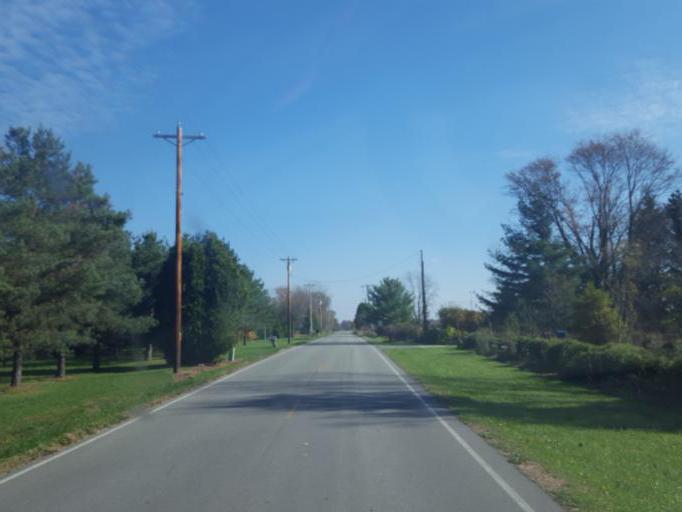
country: US
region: Ohio
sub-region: Lorain County
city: Oberlin
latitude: 41.2797
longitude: -82.2352
